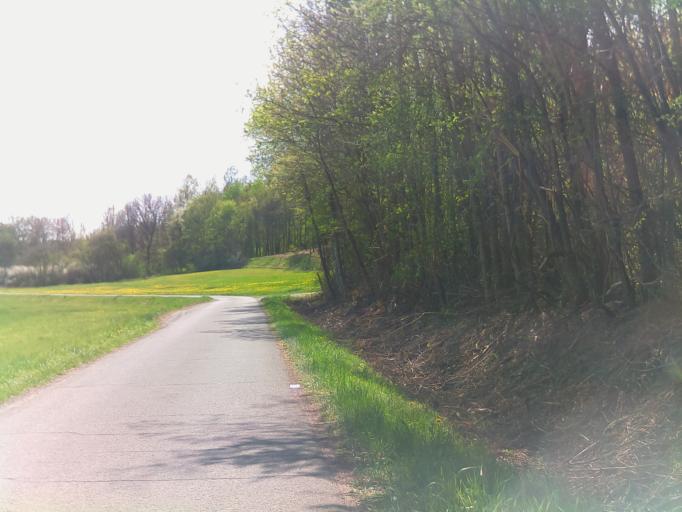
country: DE
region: Bavaria
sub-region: Upper Franconia
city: Weitramsdorf
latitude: 50.2971
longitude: 10.7919
